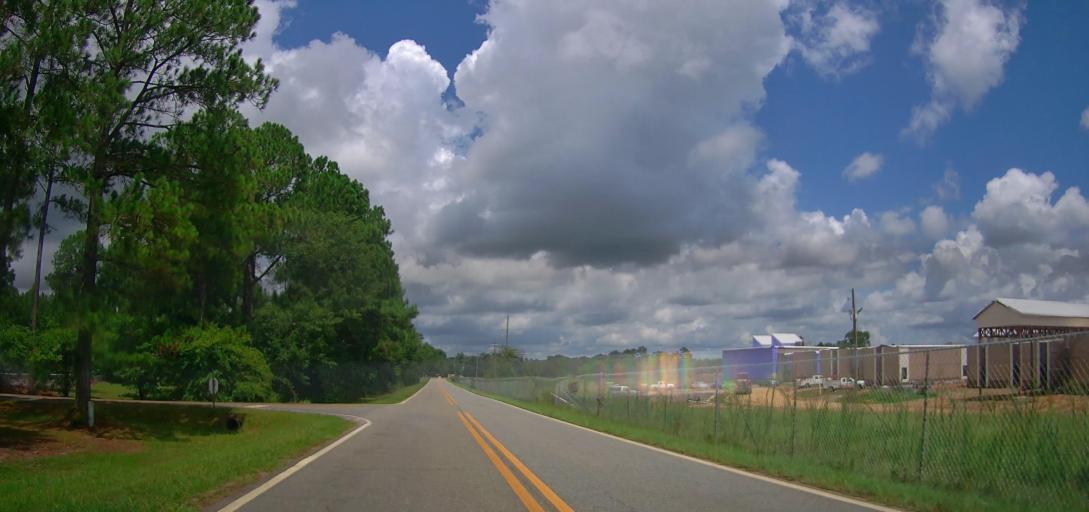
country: US
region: Georgia
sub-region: Pulaski County
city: Hawkinsville
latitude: 32.2838
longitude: -83.4921
